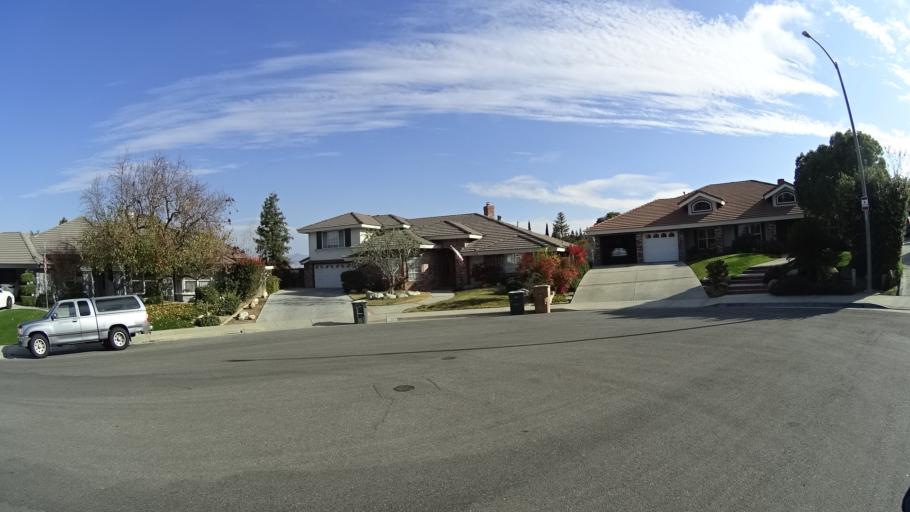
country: US
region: California
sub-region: Kern County
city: Oildale
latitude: 35.4022
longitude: -118.9175
